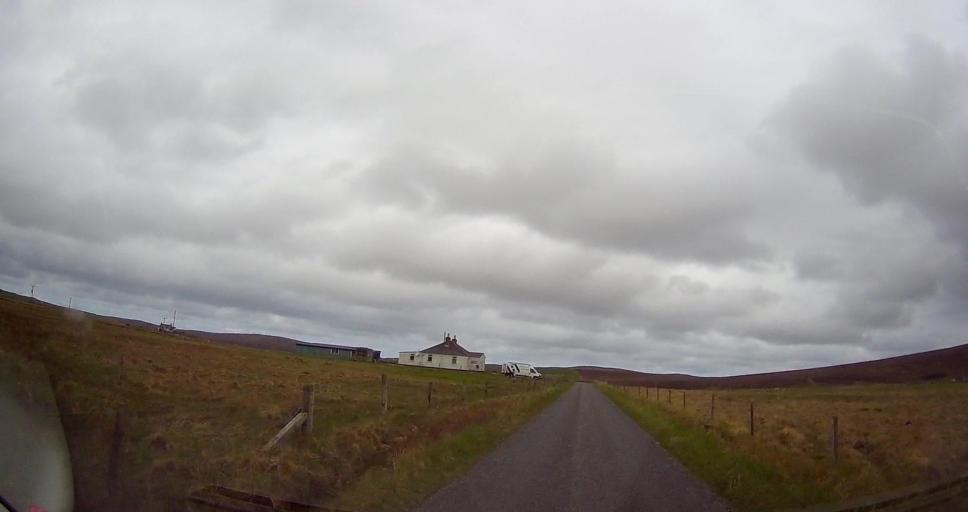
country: GB
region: Scotland
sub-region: Shetland Islands
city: Shetland
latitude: 60.7905
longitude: -0.8448
